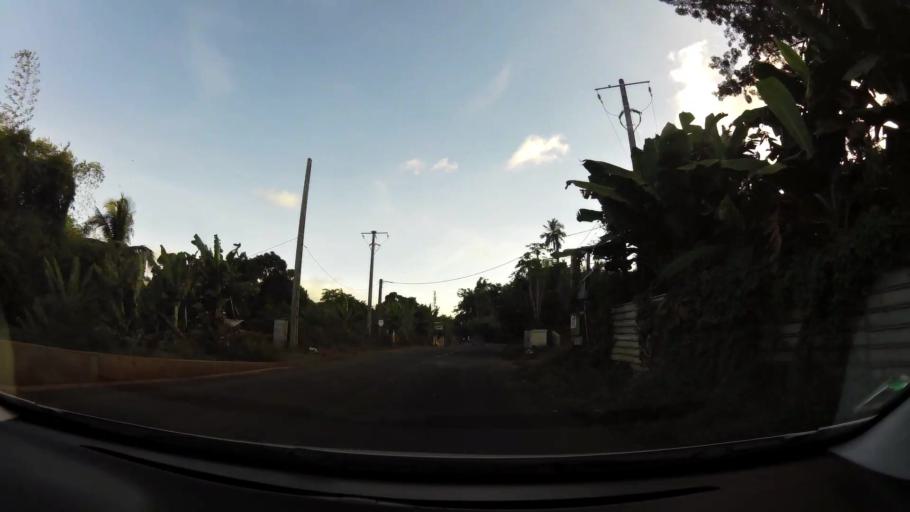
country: YT
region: Dembeni
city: Dembeni
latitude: -12.8199
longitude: 45.1959
